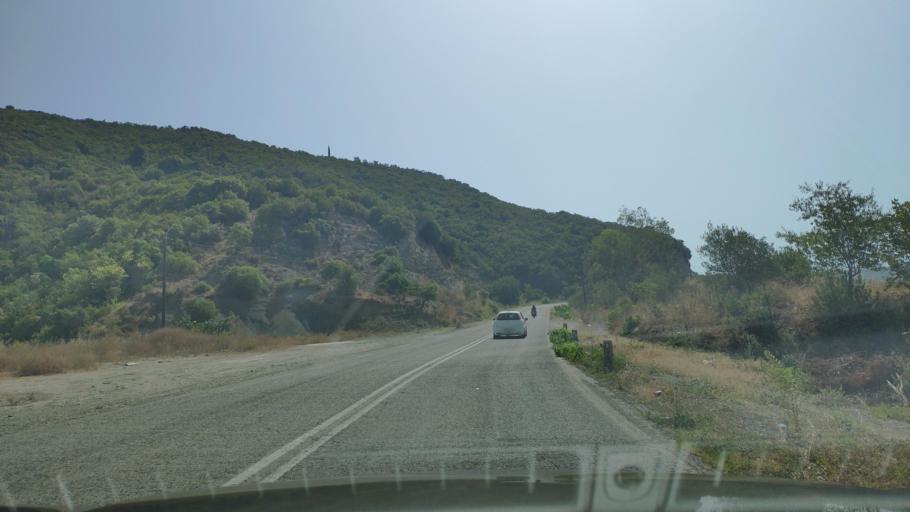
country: GR
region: Epirus
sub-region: Nomos Artas
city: Peta
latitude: 39.1691
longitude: 21.0572
